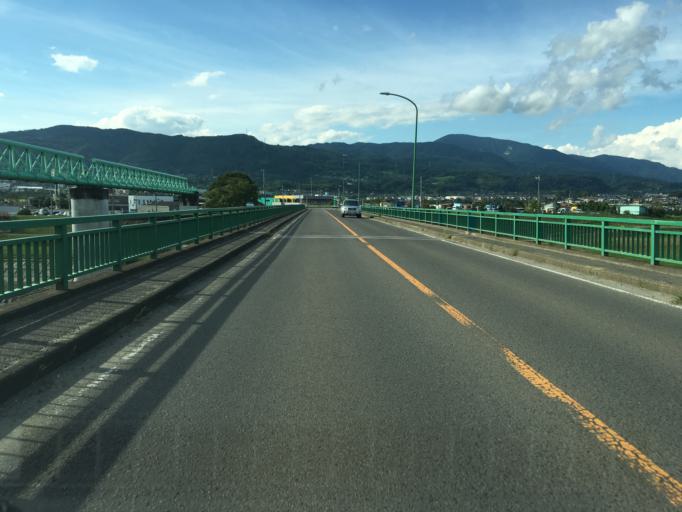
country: JP
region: Fukushima
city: Hobaramachi
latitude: 37.8291
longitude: 140.5194
